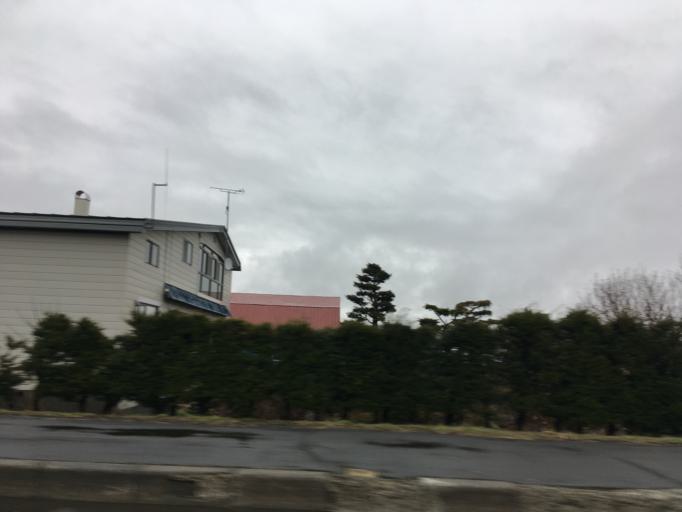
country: JP
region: Hokkaido
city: Nayoro
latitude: 44.0999
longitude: 142.4755
